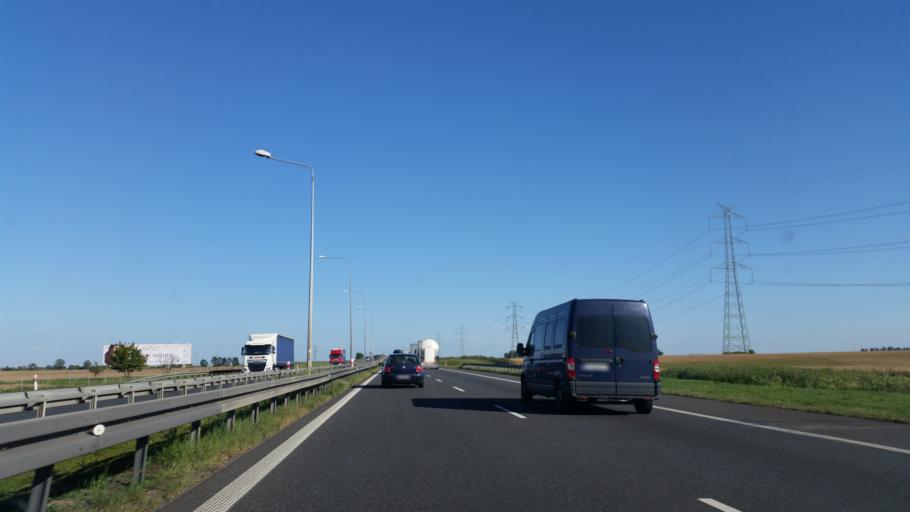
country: PL
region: Opole Voivodeship
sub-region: Powiat brzeski
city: Olszanka
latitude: 50.7534
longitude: 17.4367
